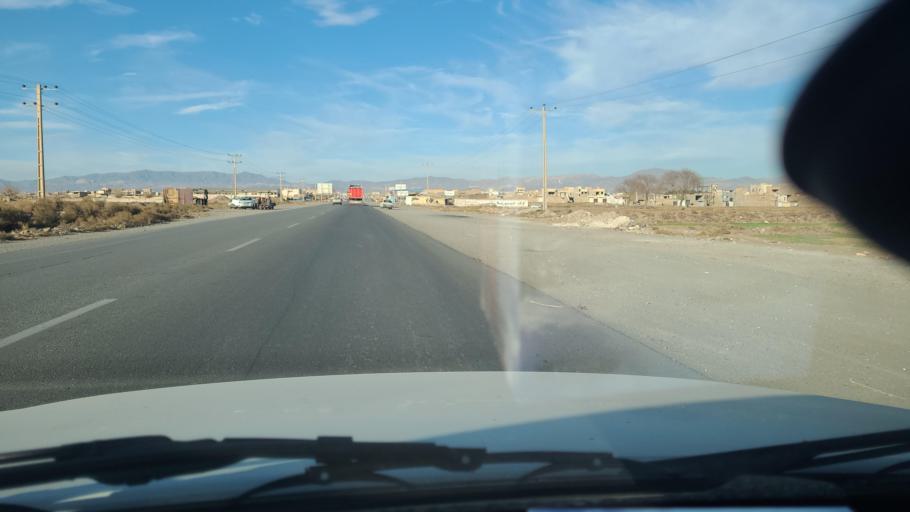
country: IR
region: Razavi Khorasan
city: Sabzevar
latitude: 36.2099
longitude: 57.6505
